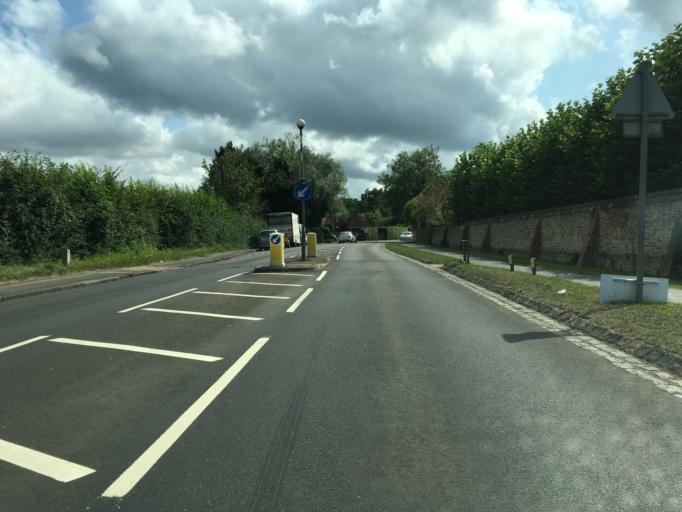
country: GB
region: England
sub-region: Kent
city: Headcorn
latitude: 51.1144
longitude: 0.6435
